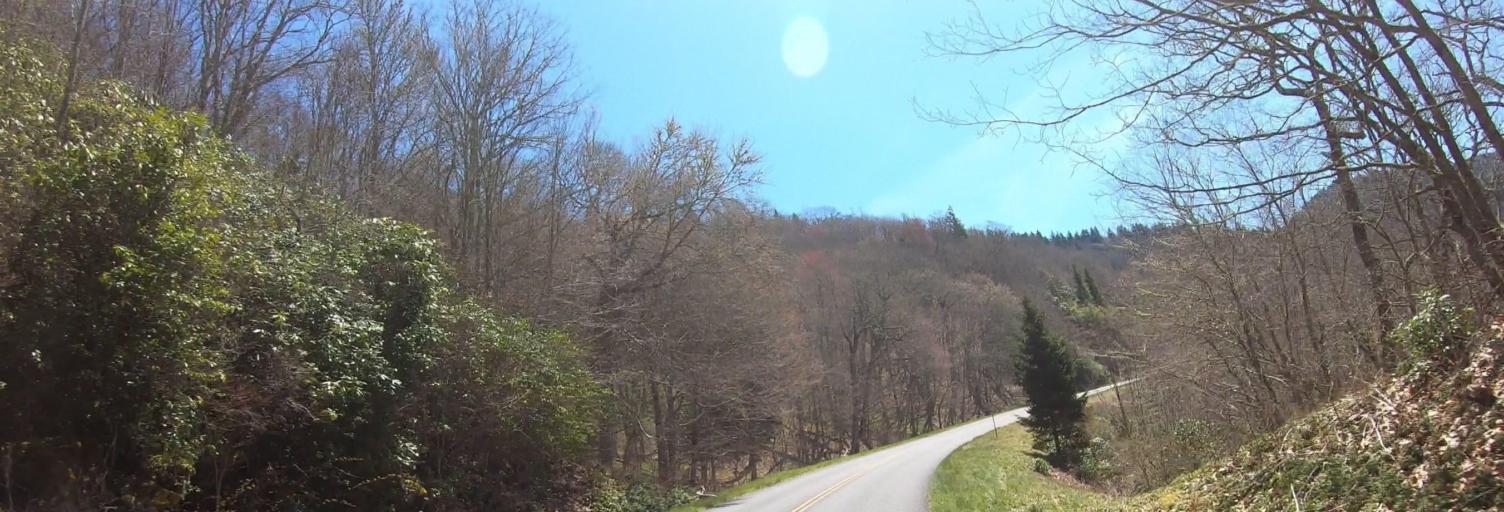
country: US
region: North Carolina
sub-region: Haywood County
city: Maggie Valley
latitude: 35.4774
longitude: -83.1458
